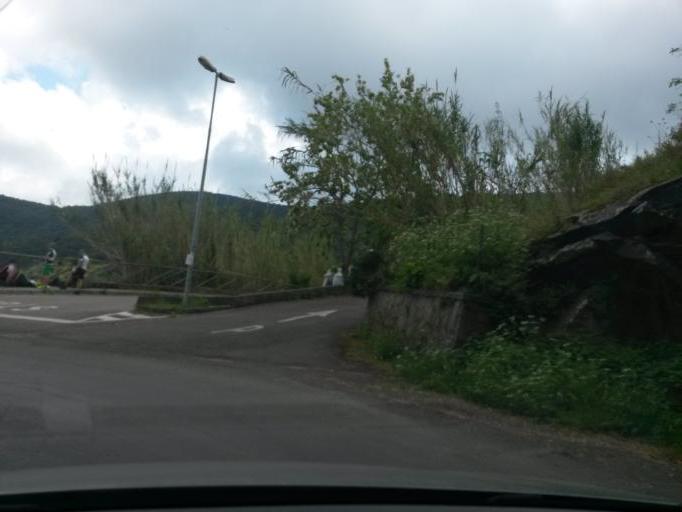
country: IT
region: Tuscany
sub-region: Provincia di Livorno
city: Marciana
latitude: 42.7859
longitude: 10.1853
